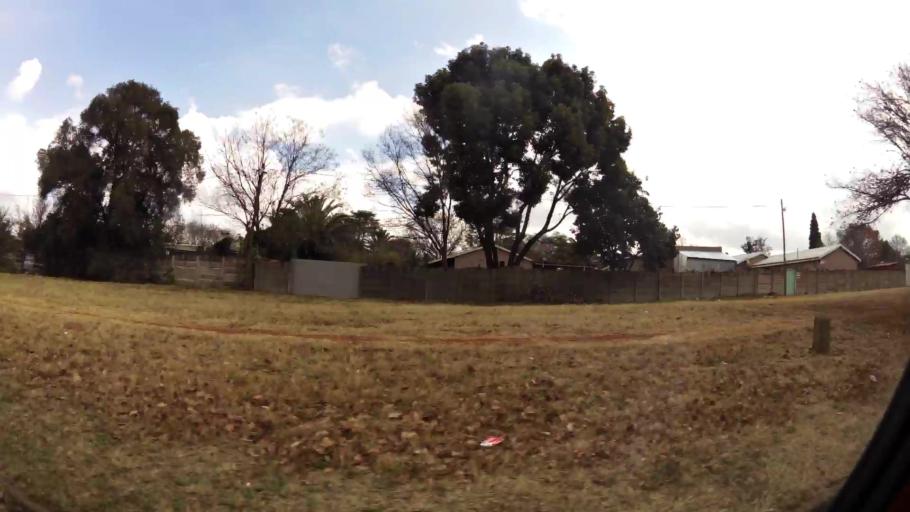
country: ZA
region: Gauteng
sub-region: Sedibeng District Municipality
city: Vanderbijlpark
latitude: -26.7308
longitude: 27.8374
